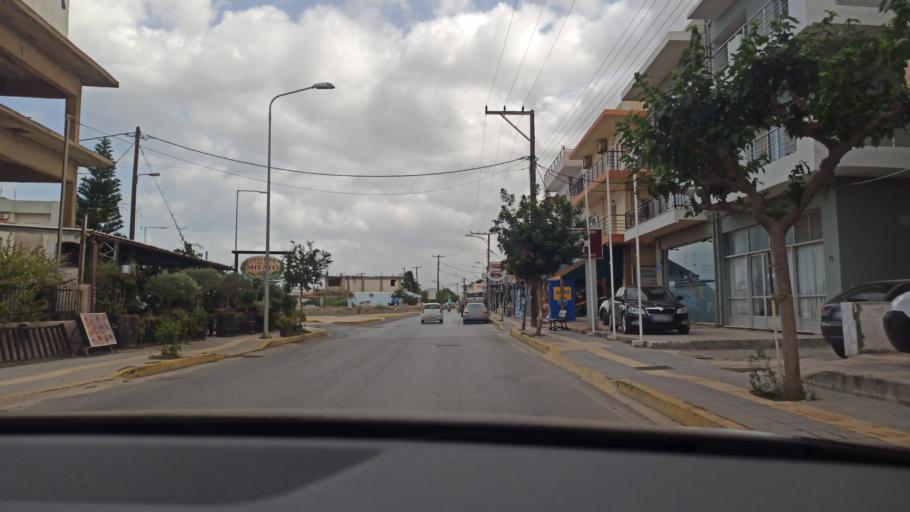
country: GR
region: Crete
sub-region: Nomos Irakleiou
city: Gazi
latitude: 35.3353
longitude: 25.0895
